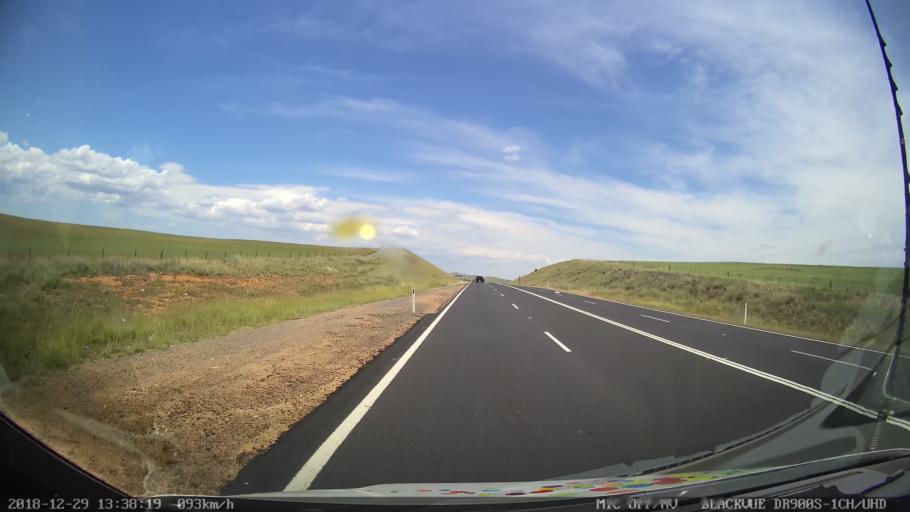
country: AU
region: New South Wales
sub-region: Cooma-Monaro
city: Cooma
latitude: -35.9968
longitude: 149.1410
